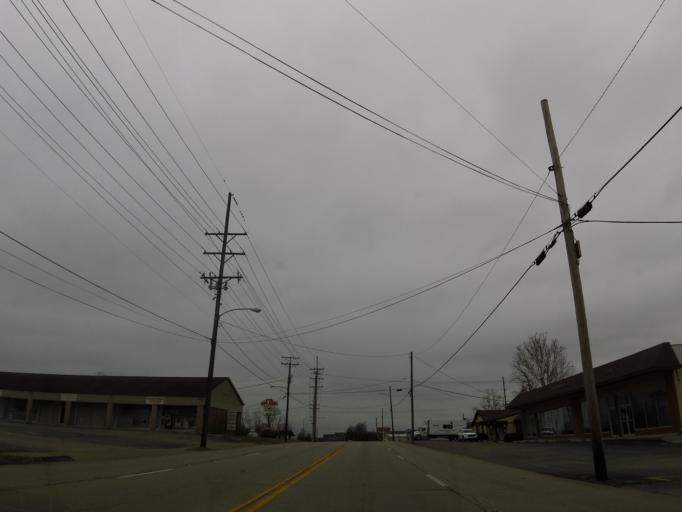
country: US
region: Kentucky
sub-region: Franklin County
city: Frankfort
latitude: 38.2024
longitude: -84.8501
